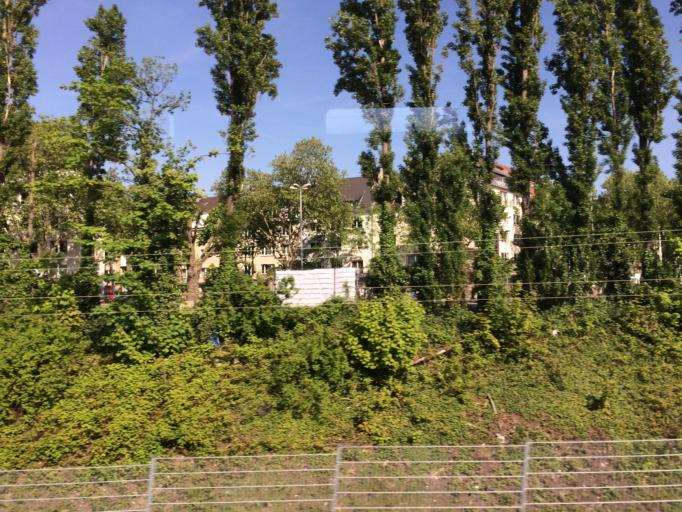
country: DE
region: North Rhine-Westphalia
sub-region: Regierungsbezirk Dusseldorf
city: Dusseldorf
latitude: 51.2382
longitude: 6.7972
